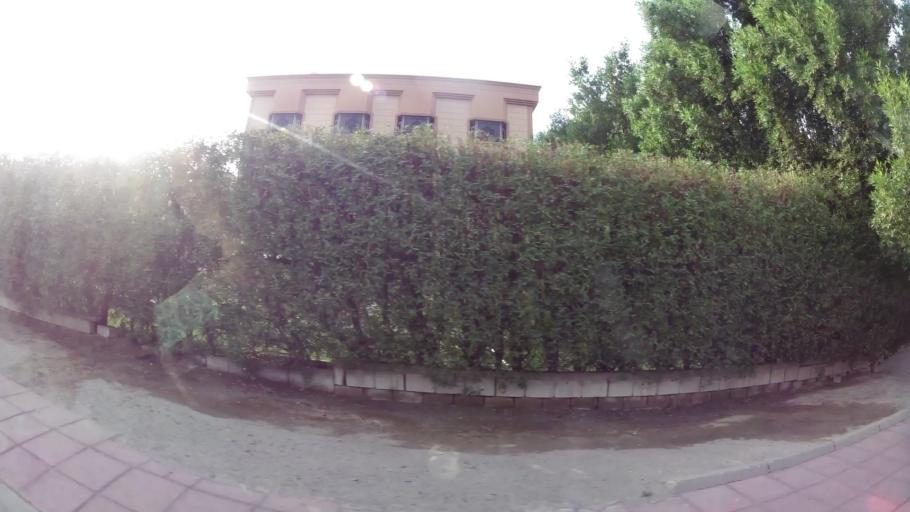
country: KW
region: Mubarak al Kabir
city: Sabah as Salim
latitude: 29.2330
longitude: 48.0620
